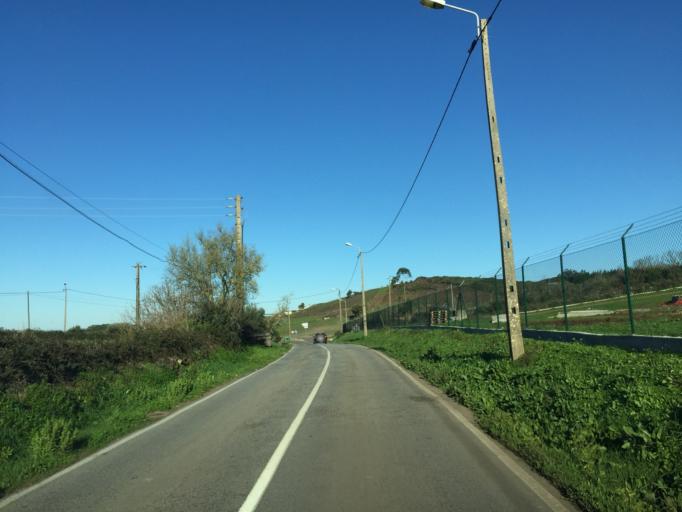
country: PT
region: Lisbon
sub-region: Sintra
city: Almargem
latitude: 38.8693
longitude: -9.2853
